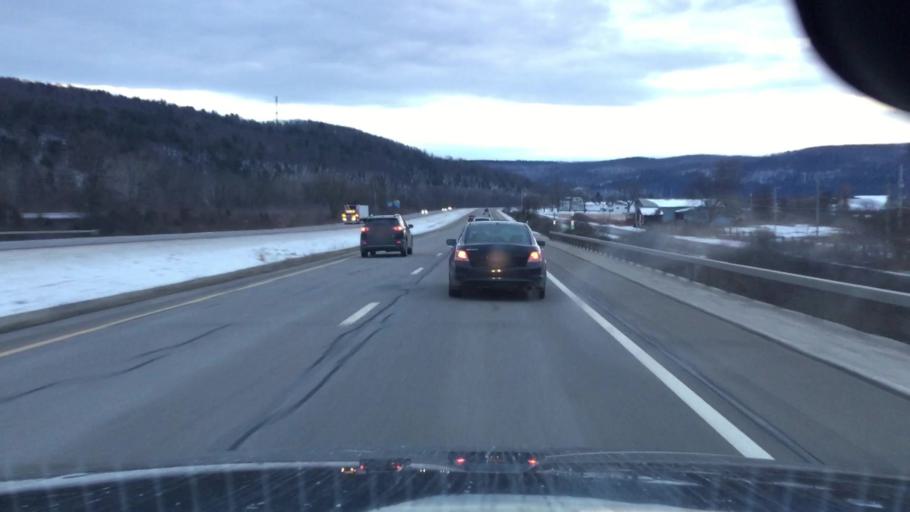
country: US
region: New York
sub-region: Steuben County
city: Gang Mills
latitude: 42.2053
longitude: -77.1684
